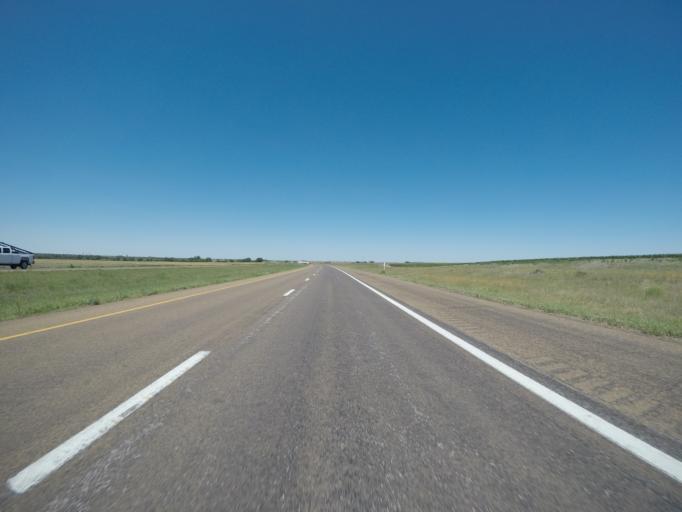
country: US
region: Kansas
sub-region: Ellis County
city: Ellis
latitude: 38.9493
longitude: -99.5230
